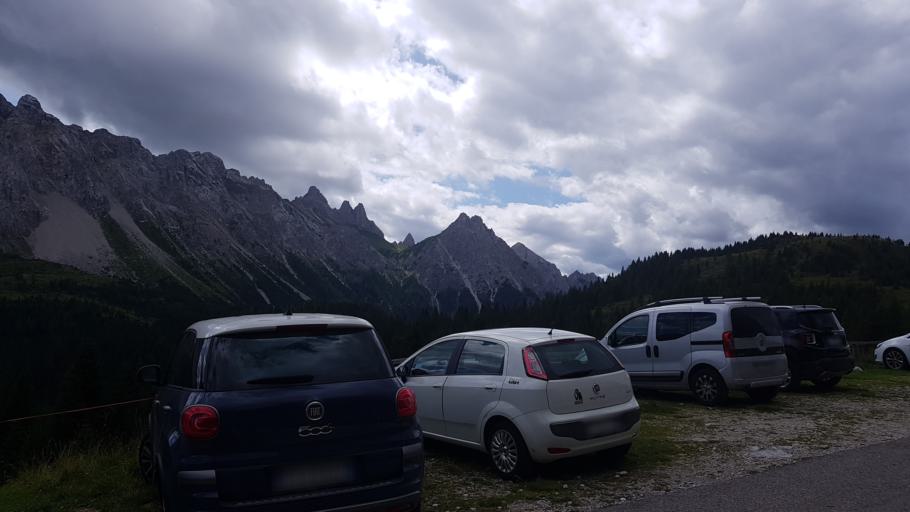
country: IT
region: Veneto
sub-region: Provincia di Belluno
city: Granvilla
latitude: 46.6202
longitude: 12.7169
